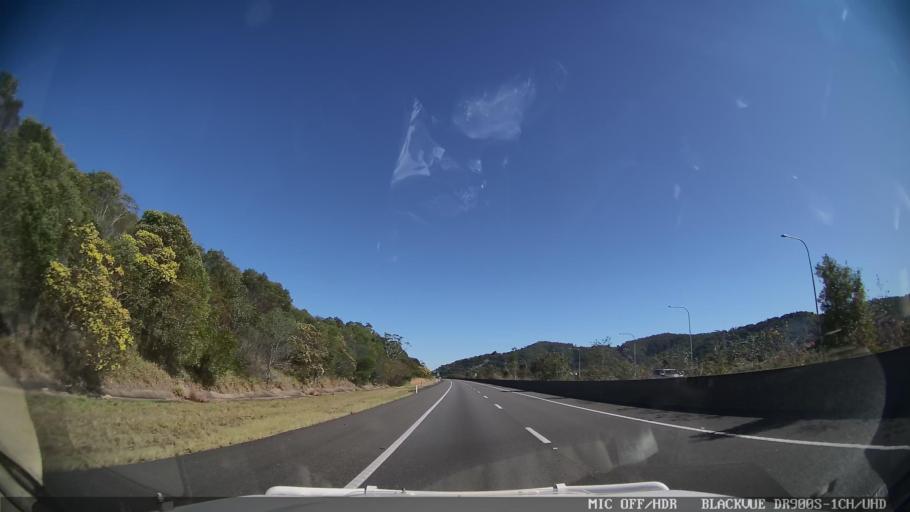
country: AU
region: Queensland
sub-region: Sunshine Coast
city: Black Mountain
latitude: -26.3903
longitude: 152.8074
